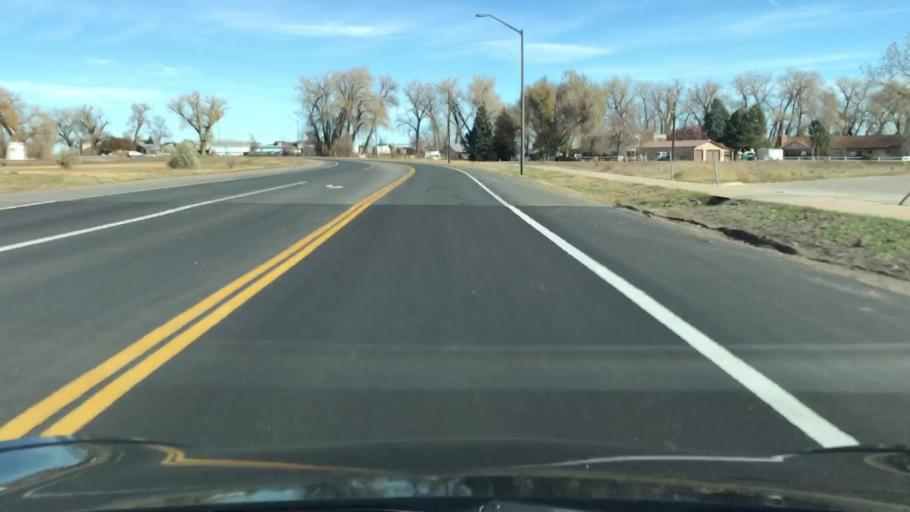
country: US
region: Colorado
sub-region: Larimer County
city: Fort Collins
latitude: 40.5858
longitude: -105.0310
